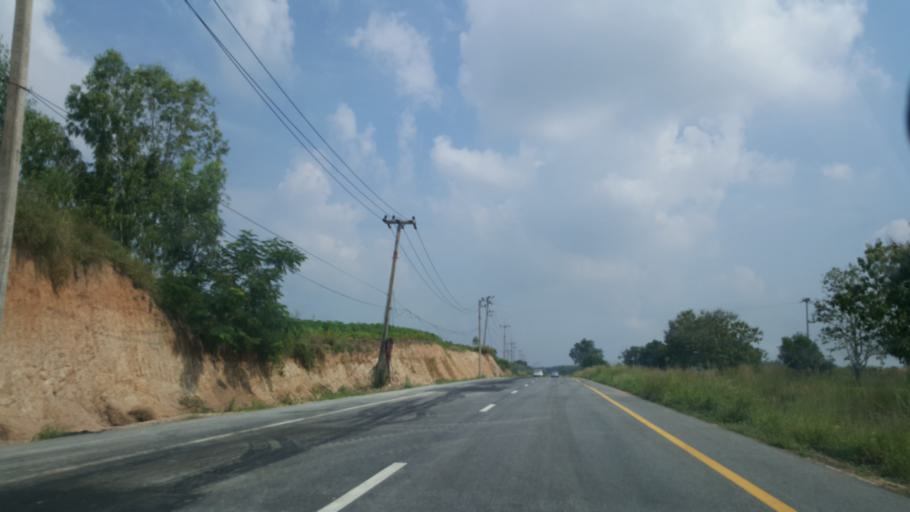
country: TH
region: Rayong
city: Ban Chang
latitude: 12.8505
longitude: 101.0170
